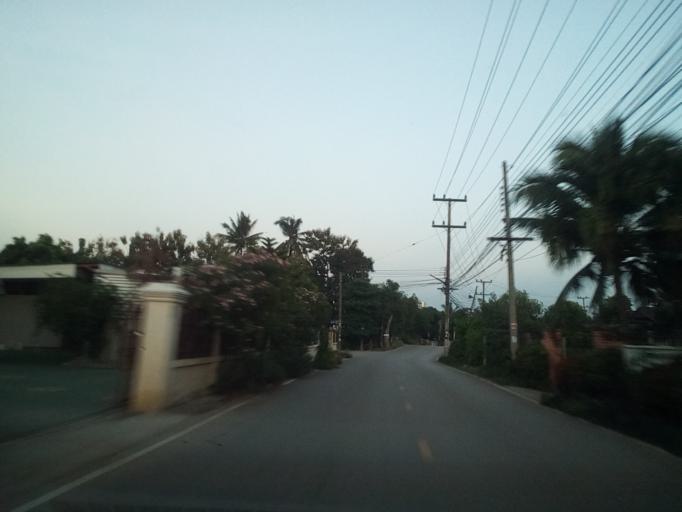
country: TH
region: Lamphun
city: Lamphun
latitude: 18.6356
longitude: 99.0463
